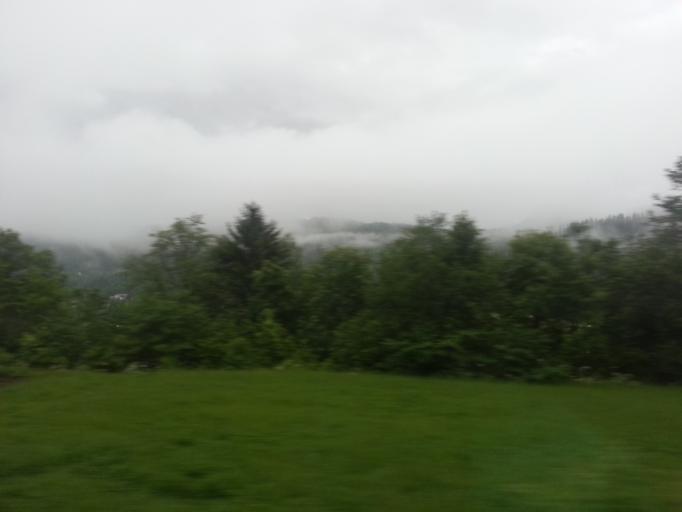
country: NO
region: Sor-Trondelag
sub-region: Midtre Gauldal
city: Storen
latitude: 63.0309
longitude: 10.2649
